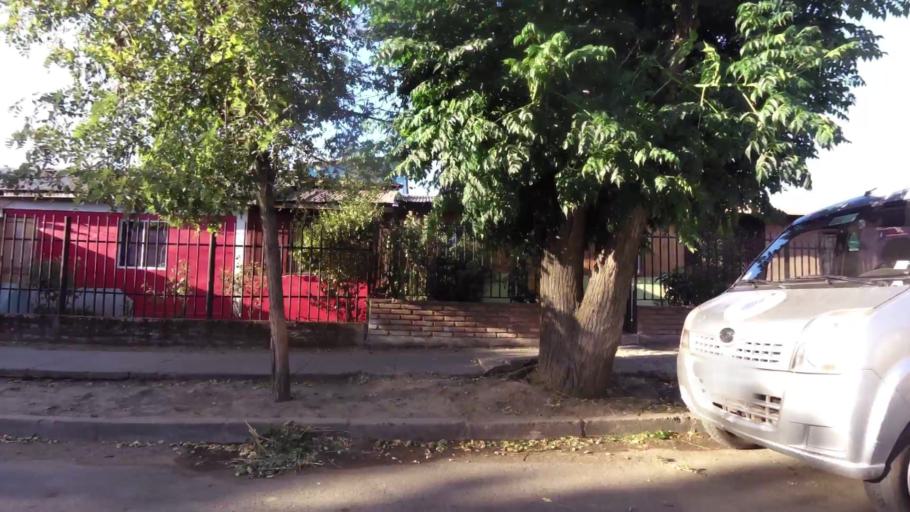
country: CL
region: Maule
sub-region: Provincia de Talca
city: Talca
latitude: -35.4393
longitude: -71.6484
